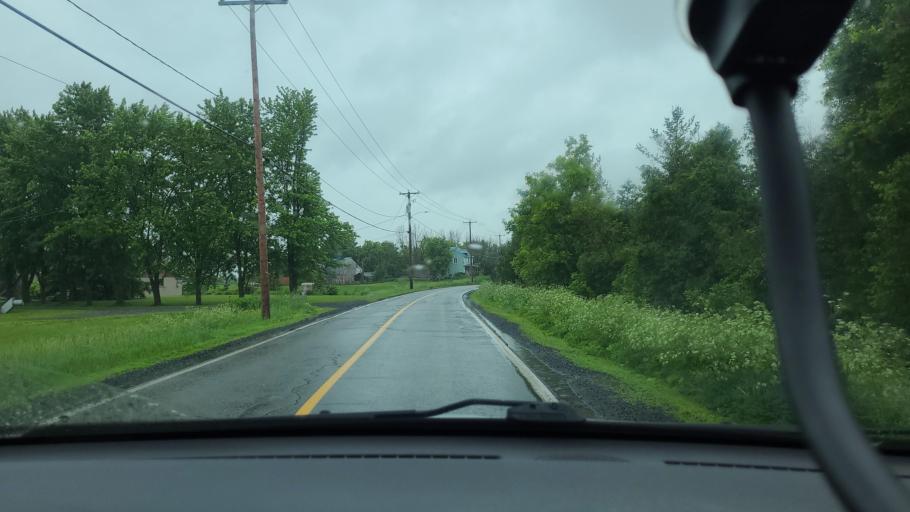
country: CA
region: Quebec
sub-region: Monteregie
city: Saint-Basile-le-Grand
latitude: 45.5494
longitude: -73.2700
